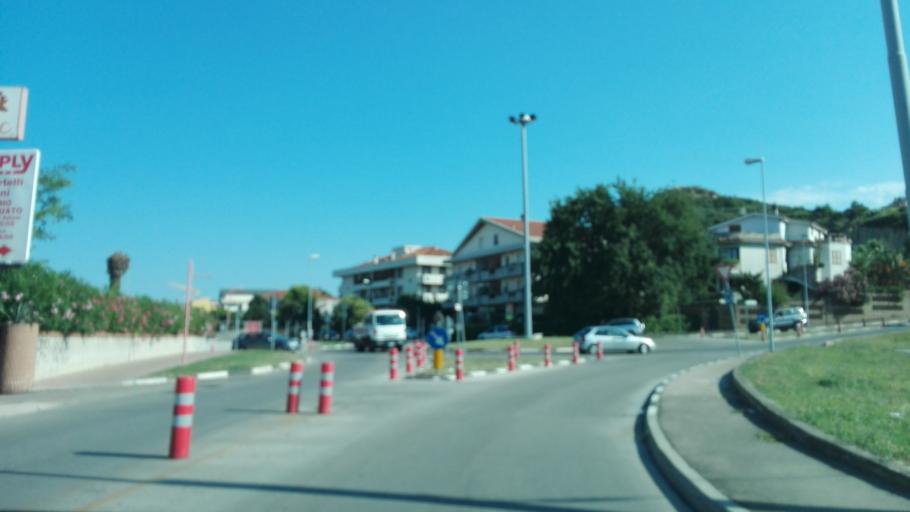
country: IT
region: Abruzzo
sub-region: Provincia di Pescara
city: Montesilvano Marina
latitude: 42.5108
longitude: 14.1530
